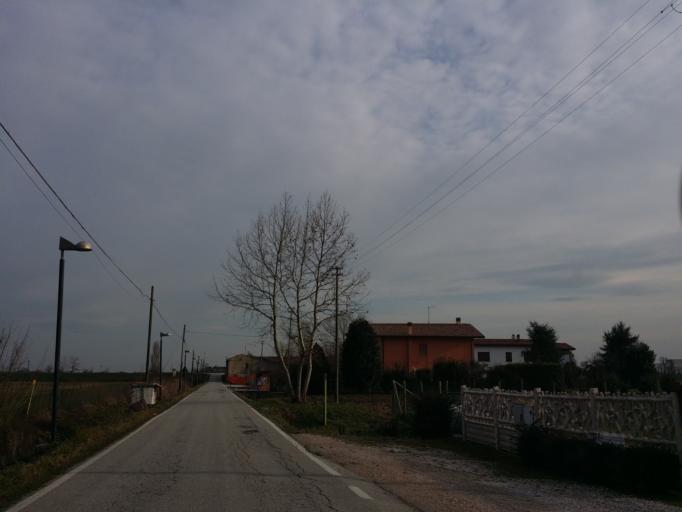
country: IT
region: Veneto
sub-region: Provincia di Padova
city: Terradura
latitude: 45.3485
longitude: 11.8266
